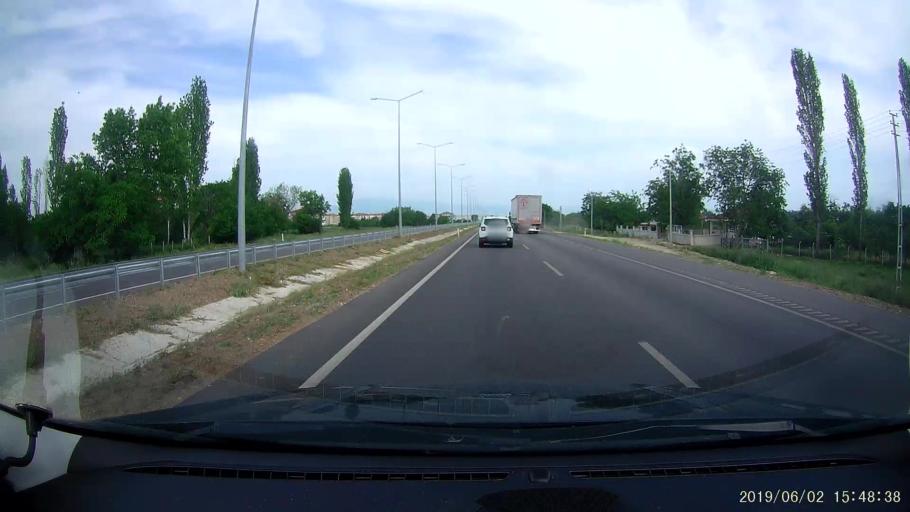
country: TR
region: Amasya
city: Merzifon
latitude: 40.8615
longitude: 35.4456
